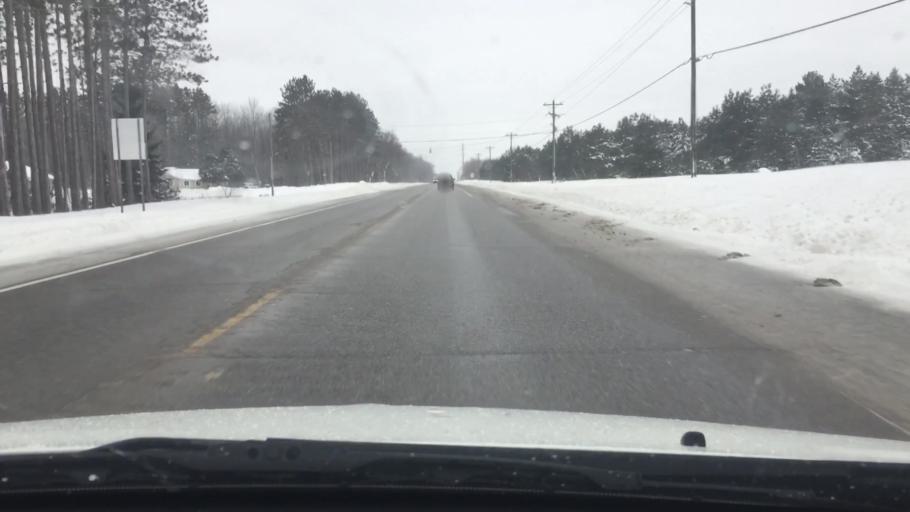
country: US
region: Michigan
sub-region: Otsego County
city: Gaylord
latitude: 45.0277
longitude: -84.7446
